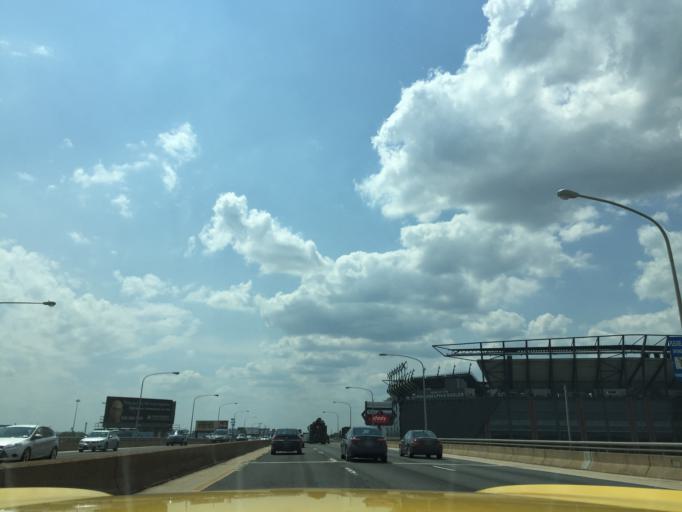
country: US
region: New Jersey
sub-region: Gloucester County
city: National Park
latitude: 39.8997
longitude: -75.1629
